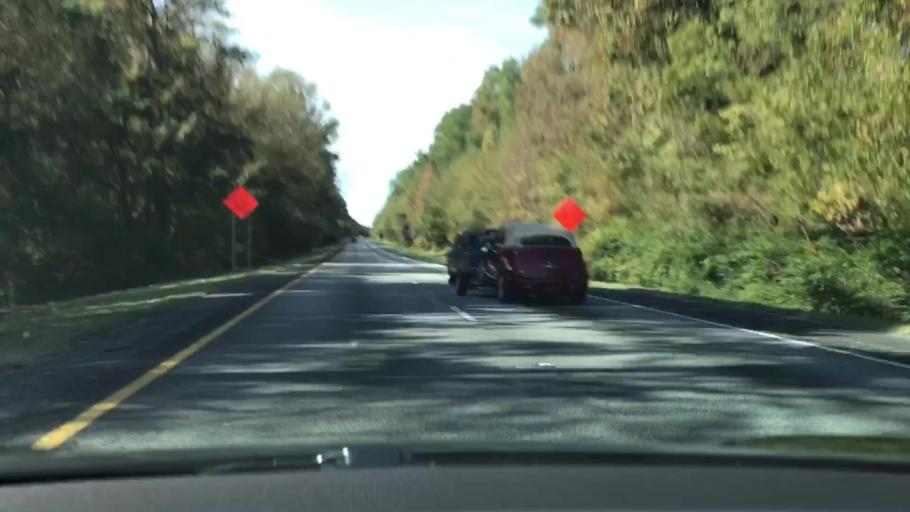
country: US
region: Georgia
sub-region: Morgan County
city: Madison
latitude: 33.5773
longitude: -83.5518
